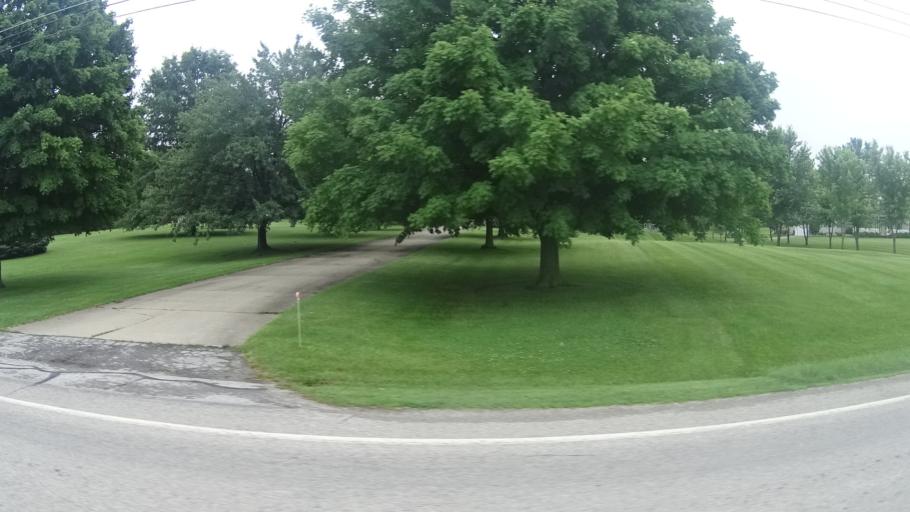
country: US
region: Ohio
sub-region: Erie County
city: Milan
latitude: 41.3356
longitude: -82.5915
